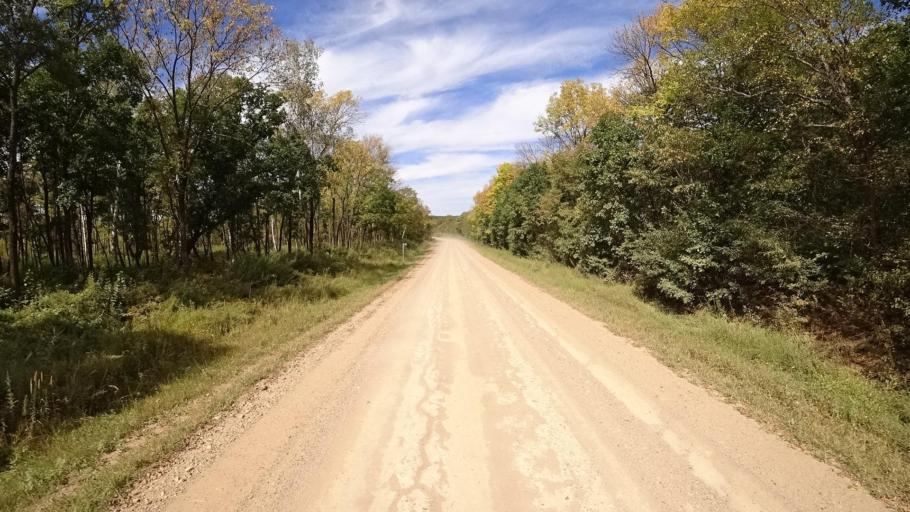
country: RU
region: Primorskiy
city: Yakovlevka
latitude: 44.6322
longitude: 133.6009
